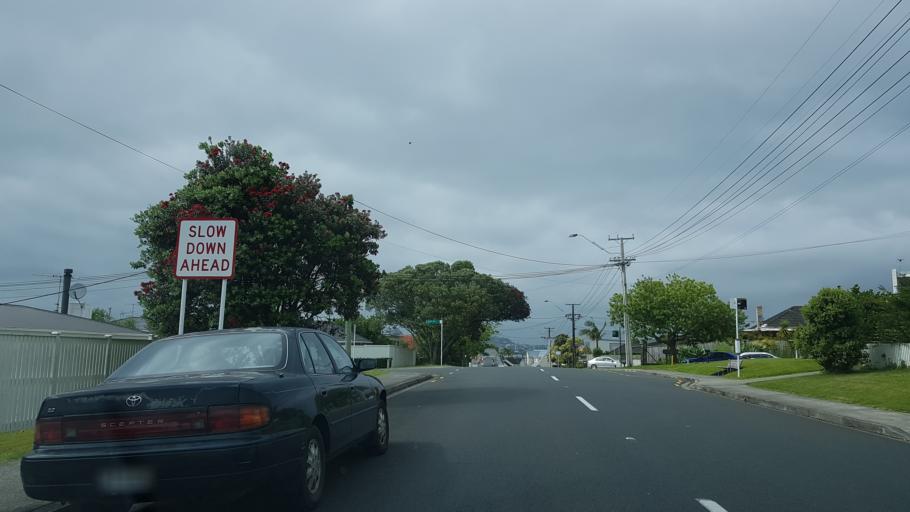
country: NZ
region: Auckland
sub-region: Auckland
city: North Shore
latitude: -36.8081
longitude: 174.7543
